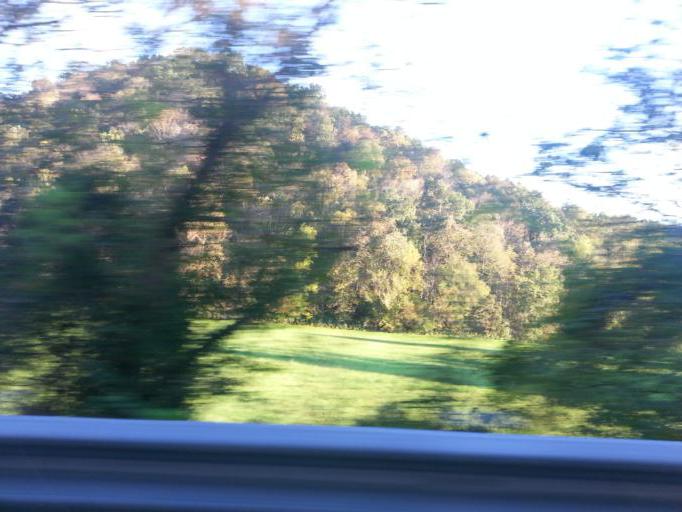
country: US
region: Tennessee
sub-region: Blount County
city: Wildwood
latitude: 35.6886
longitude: -83.7180
